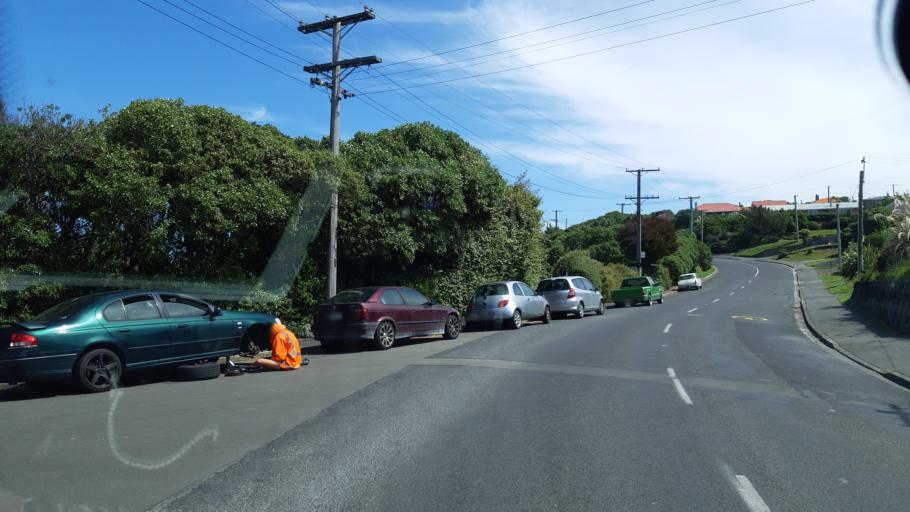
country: NZ
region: Otago
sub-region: Dunedin City
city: Dunedin
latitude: -45.9039
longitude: 170.5372
